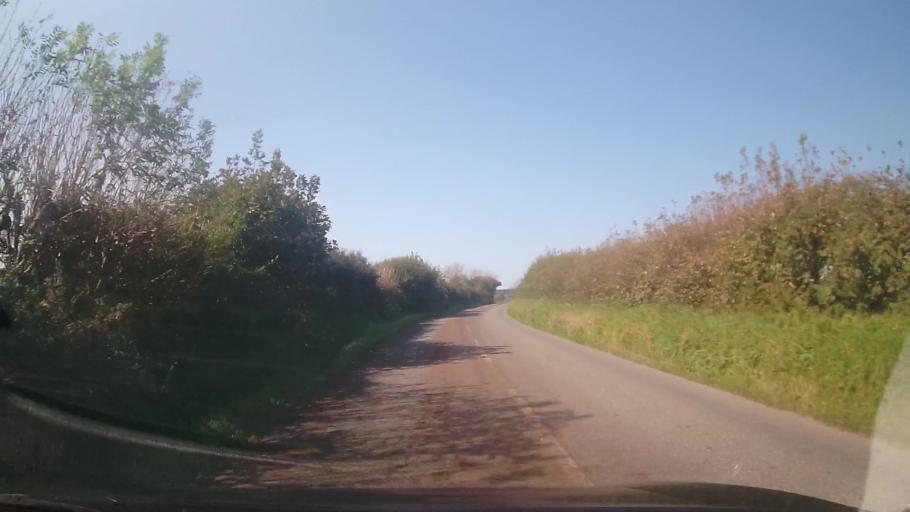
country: GB
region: Wales
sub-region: Pembrokeshire
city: Camrose
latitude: 51.8437
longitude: -5.0024
